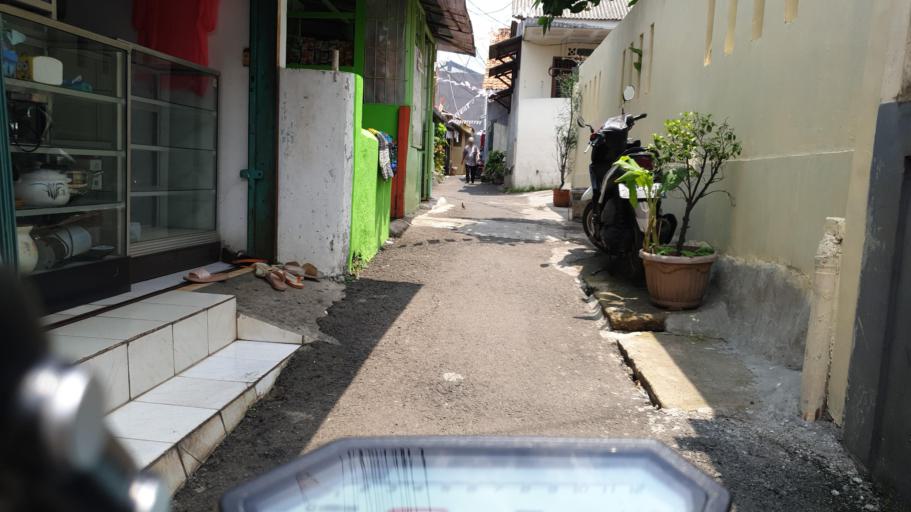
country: ID
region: West Java
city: Depok
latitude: -6.3334
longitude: 106.8305
